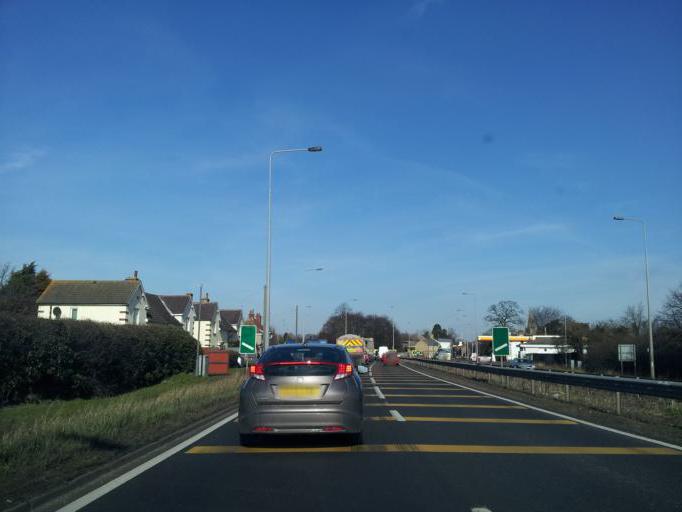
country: GB
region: England
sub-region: Cambridgeshire
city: Buckden
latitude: 52.2904
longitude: -0.2571
